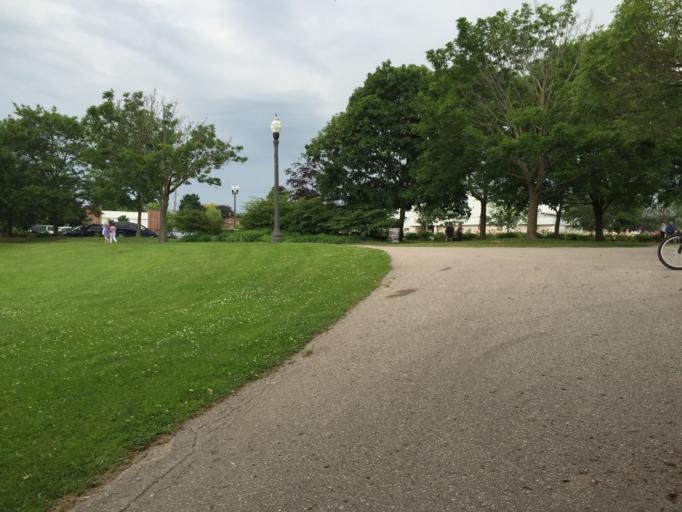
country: CA
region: Ontario
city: Oshawa
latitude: 43.8996
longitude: -78.8707
